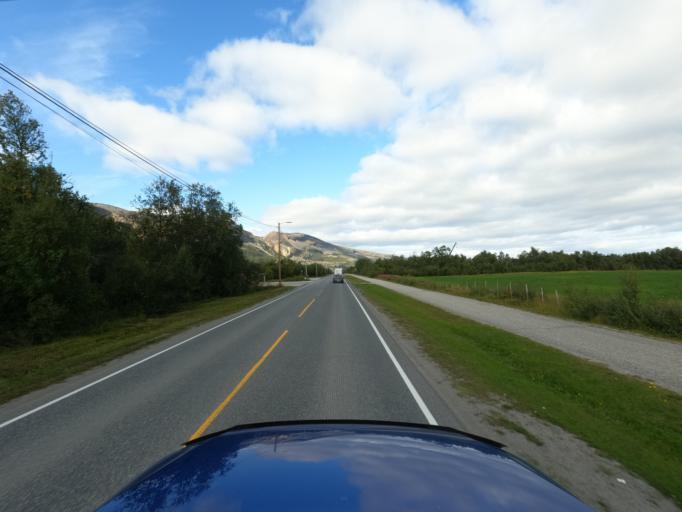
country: NO
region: Finnmark Fylke
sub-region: Porsanger
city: Lakselv
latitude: 70.0552
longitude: 24.9389
